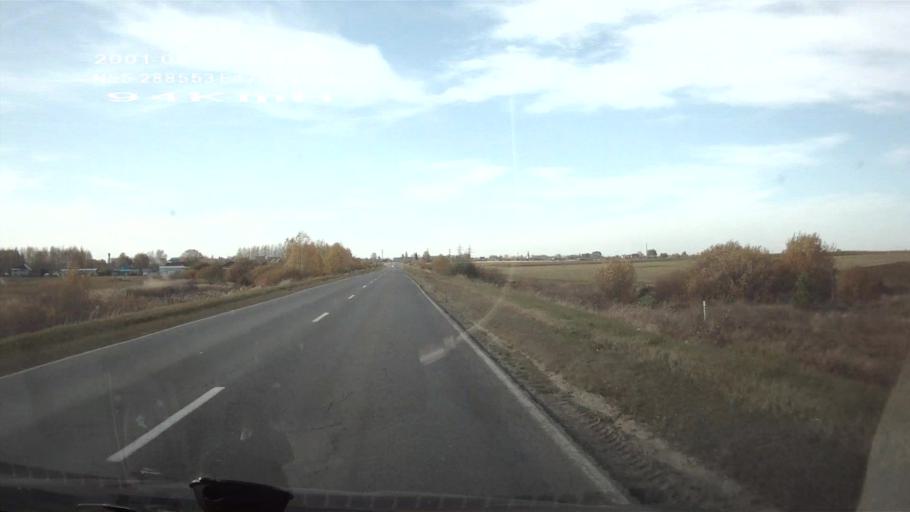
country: RU
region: Chuvashia
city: Ibresi
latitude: 55.2886
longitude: 47.0694
